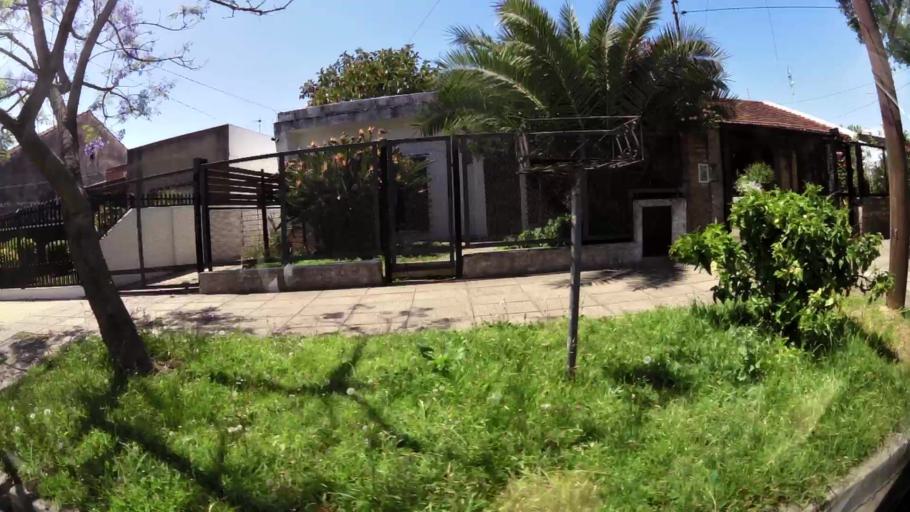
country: AR
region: Buenos Aires
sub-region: Partido de Merlo
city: Merlo
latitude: -34.6747
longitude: -58.6883
